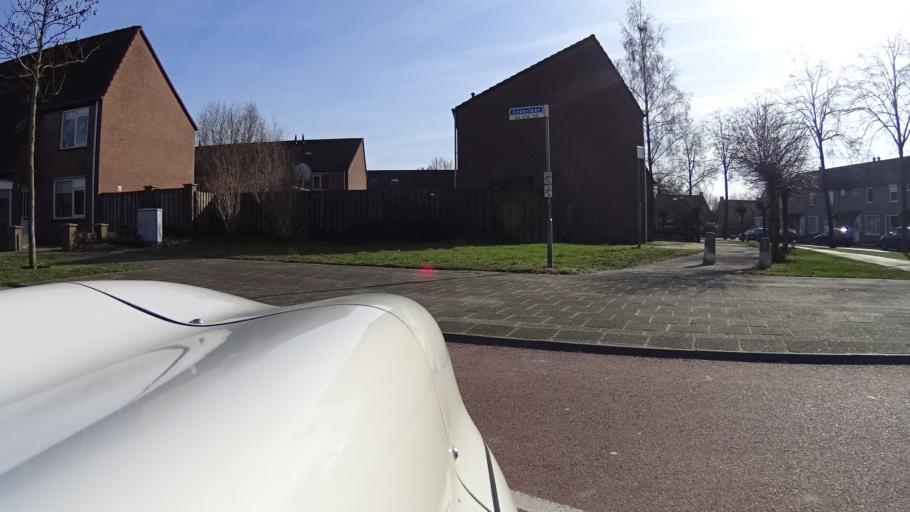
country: NL
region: North Brabant
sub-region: Gemeente Veghel
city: Veghel
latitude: 51.6231
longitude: 5.5600
